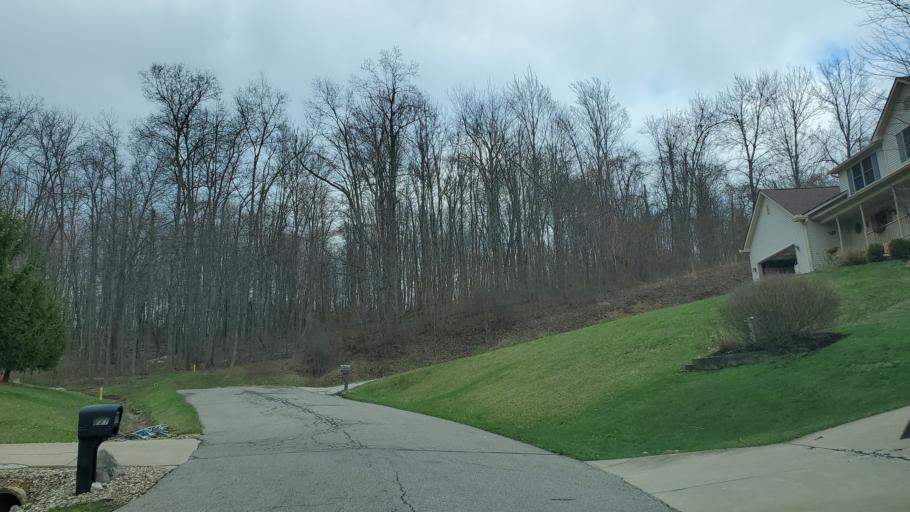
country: US
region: Ohio
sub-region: Licking County
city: Newark
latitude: 40.0338
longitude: -82.3762
